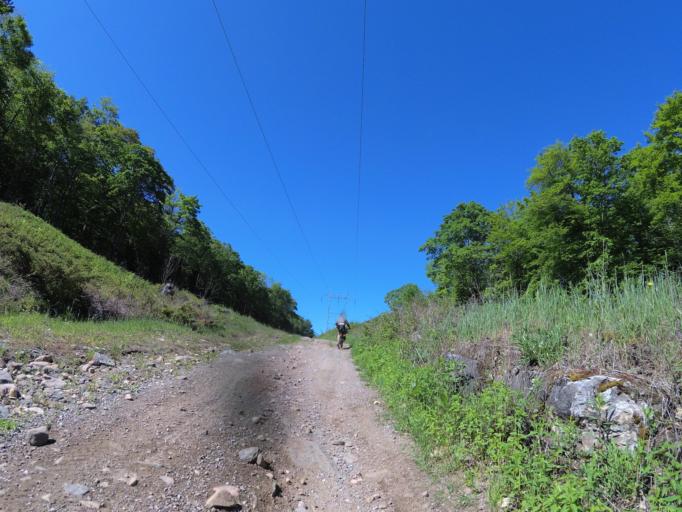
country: CA
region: Ontario
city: Renfrew
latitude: 45.0903
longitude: -77.0817
